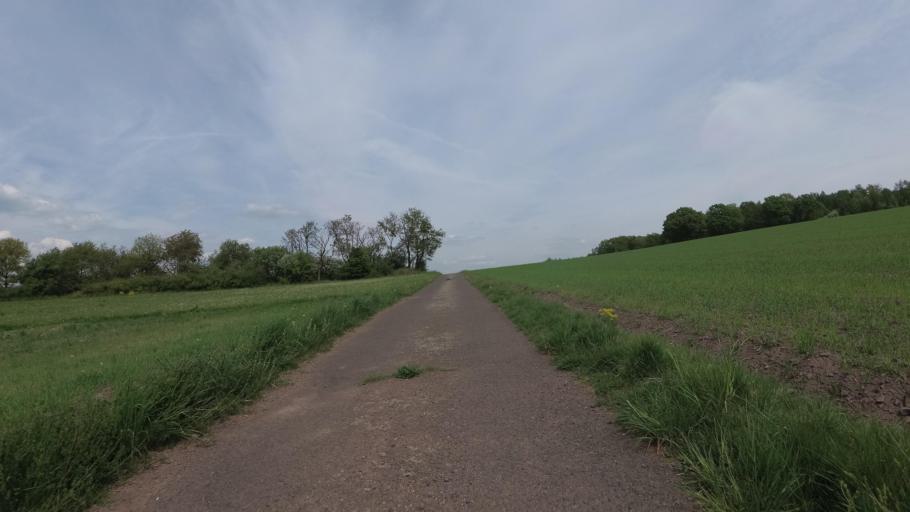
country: DE
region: Rheinland-Pfalz
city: Eckersweiler
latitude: 49.5668
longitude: 7.2989
